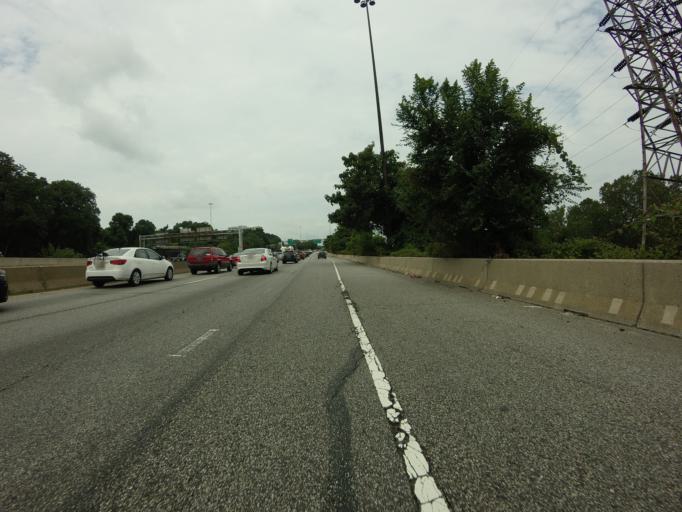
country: US
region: Pennsylvania
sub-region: Montgomery County
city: Bala-Cynwyd
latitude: 40.0074
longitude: -75.2000
